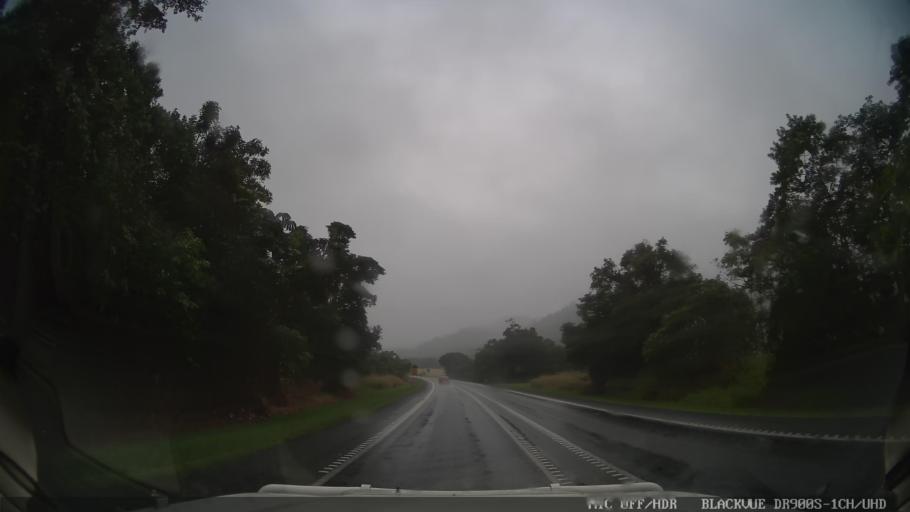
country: AU
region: Queensland
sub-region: Cassowary Coast
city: Innisfail
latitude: -17.8622
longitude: 145.9855
